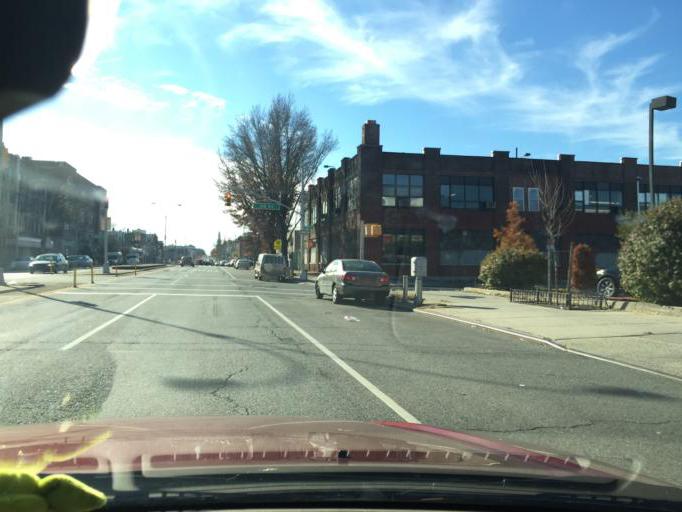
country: US
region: New York
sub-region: Kings County
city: Brooklyn
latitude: 40.6592
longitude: -73.9996
